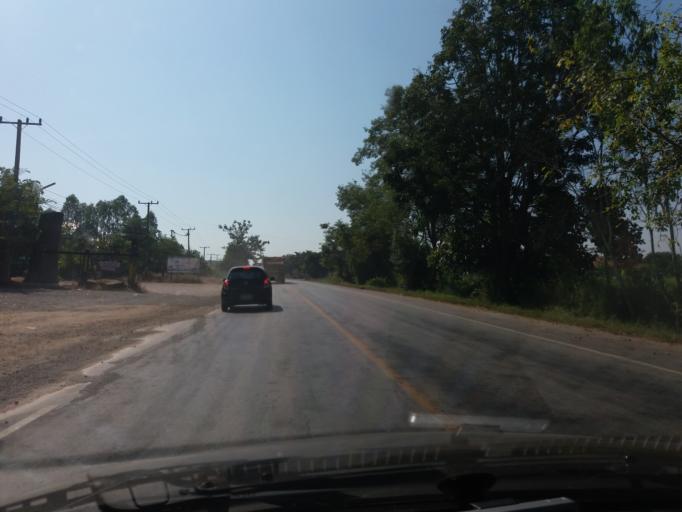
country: TH
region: Kamphaeng Phet
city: Khlong Khlung
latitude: 16.1618
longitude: 99.8031
